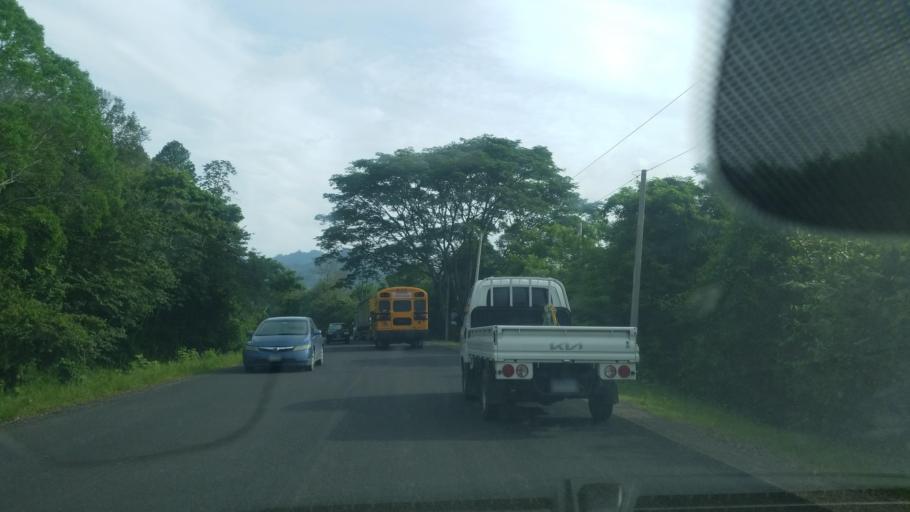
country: HN
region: Santa Barbara
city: Petoa
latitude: 15.2080
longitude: -88.2691
